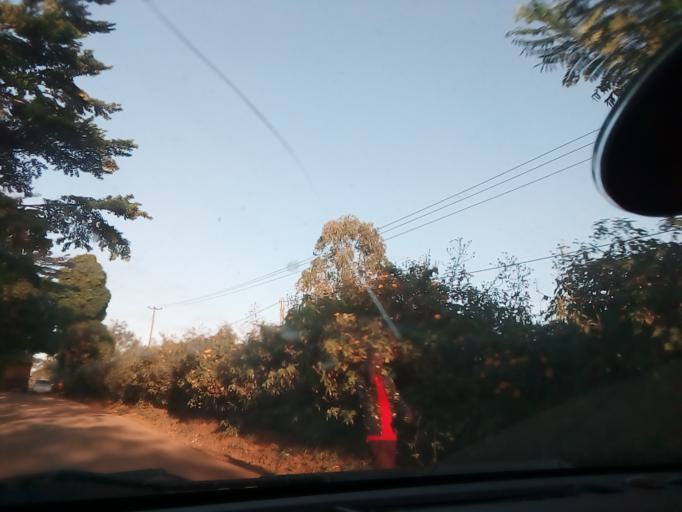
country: UG
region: Central Region
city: Masaka
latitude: -0.3300
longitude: 31.7558
